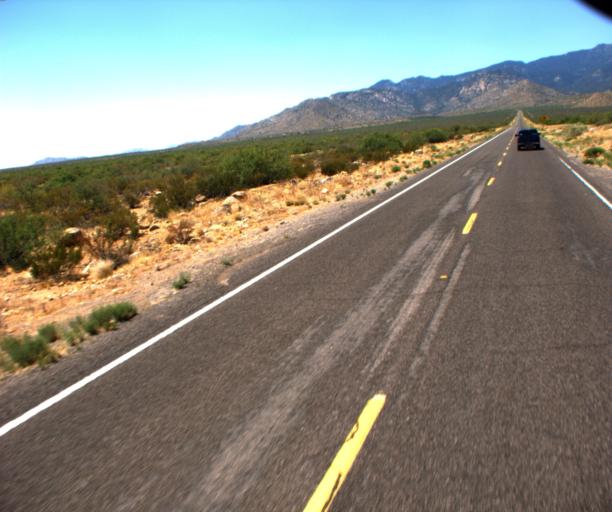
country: US
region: Arizona
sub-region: Graham County
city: Swift Trail Junction
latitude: 32.7128
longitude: -109.7315
